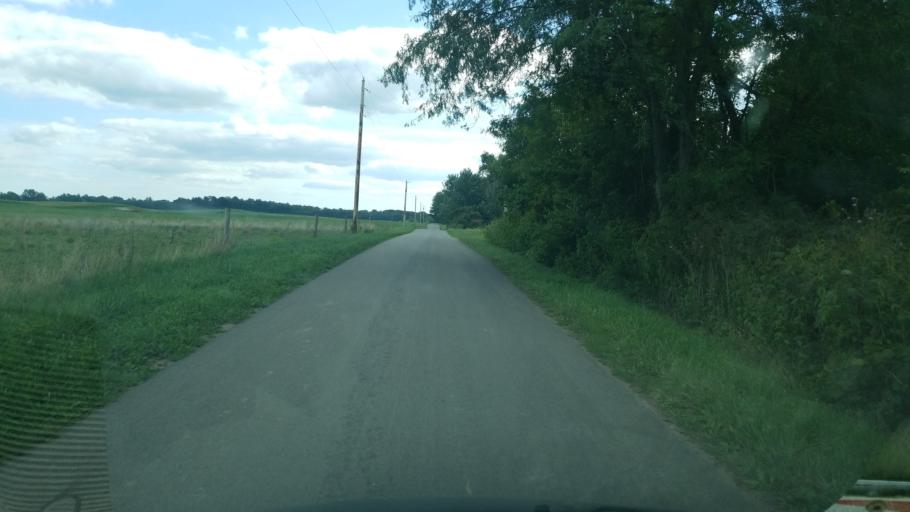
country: US
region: Ohio
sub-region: Logan County
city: De Graff
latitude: 40.3694
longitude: -83.8883
